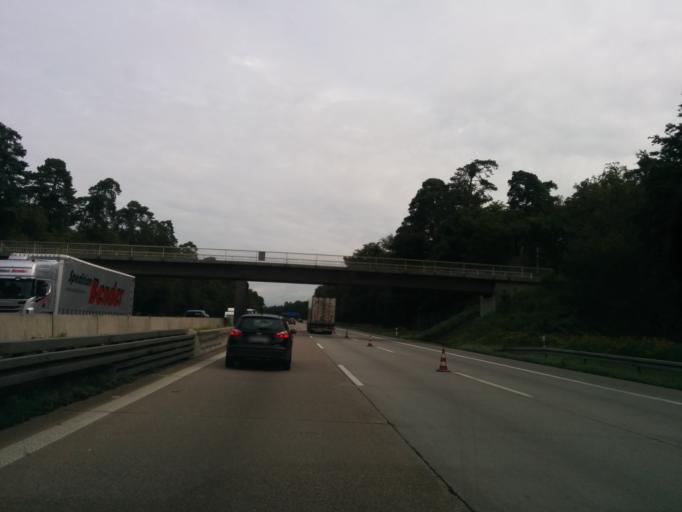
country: DE
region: Baden-Wuerttemberg
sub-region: Karlsruhe Region
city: Kronau
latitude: 49.2095
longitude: 8.5989
